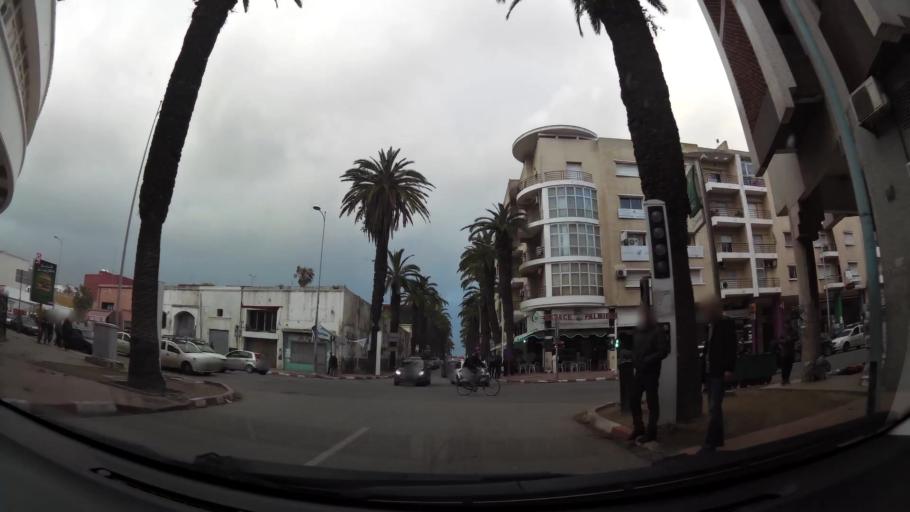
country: MA
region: Doukkala-Abda
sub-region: El-Jadida
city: El Jadida
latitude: 33.2483
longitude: -8.5012
